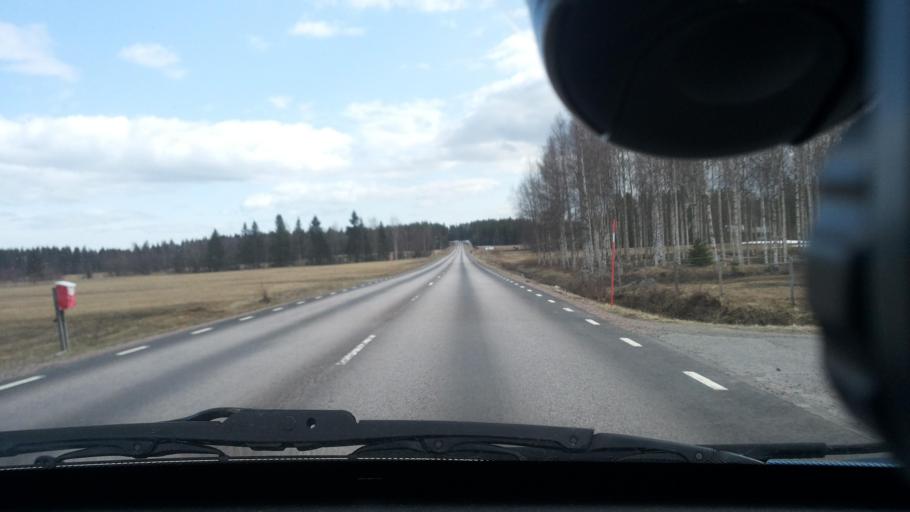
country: SE
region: Norrbotten
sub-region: Lulea Kommun
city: Sodra Sunderbyn
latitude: 65.6137
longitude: 21.9518
